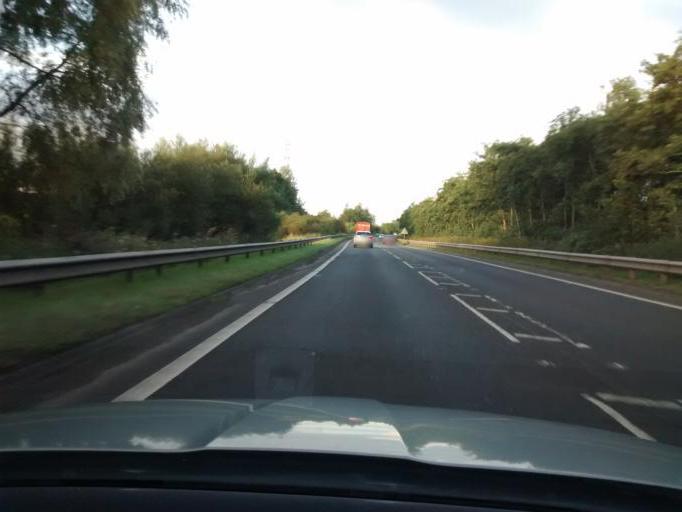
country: GB
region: Scotland
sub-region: Renfrewshire
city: Howwood
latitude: 55.8167
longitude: -4.5503
